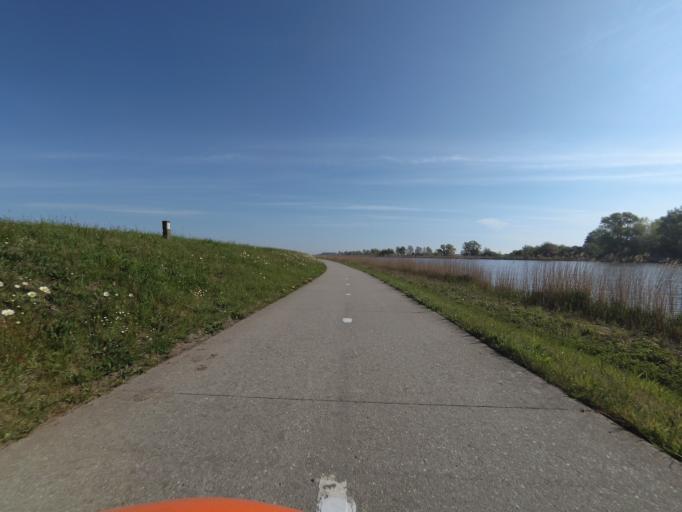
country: NL
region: Gelderland
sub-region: Gemeente Elburg
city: Elburg
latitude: 52.4614
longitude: 5.8196
